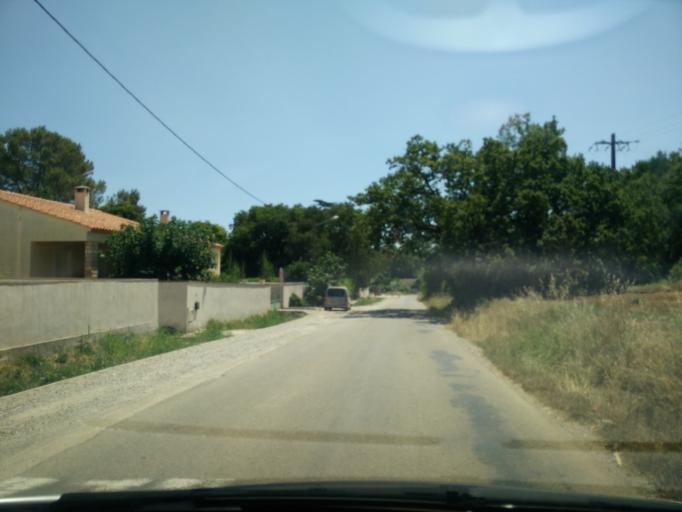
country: FR
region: Languedoc-Roussillon
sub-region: Departement de l'Herault
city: Saint-Christol
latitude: 43.7249
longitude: 4.0748
